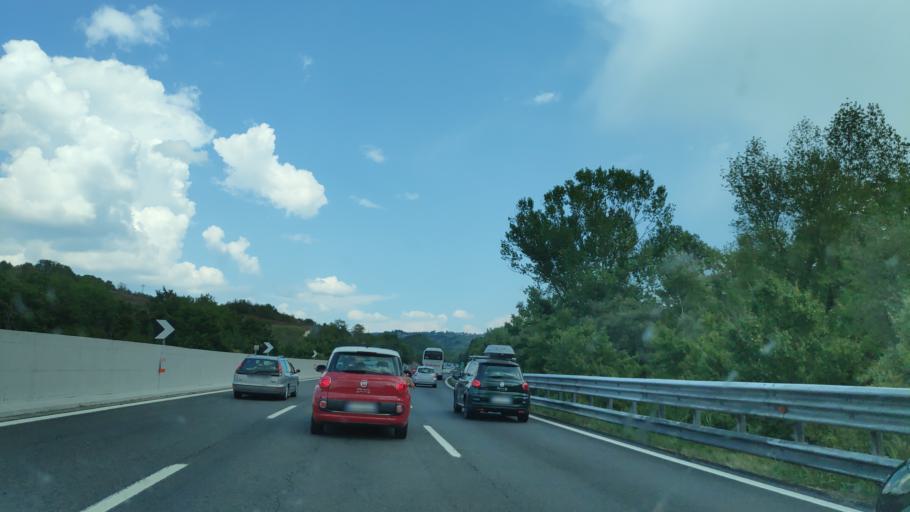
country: IT
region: Umbria
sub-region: Provincia di Terni
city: Stazione di Allerona
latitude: 42.8190
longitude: 12.0335
